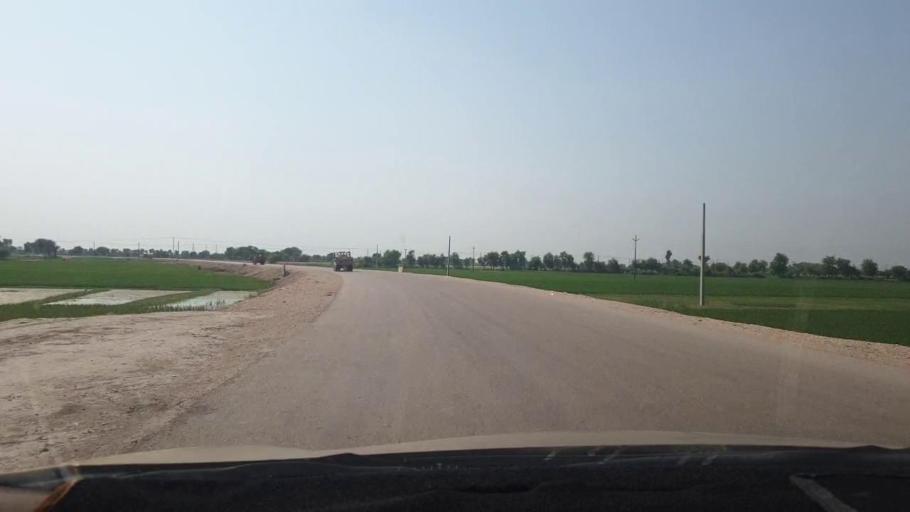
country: PK
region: Sindh
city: Larkana
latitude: 27.6105
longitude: 68.2370
